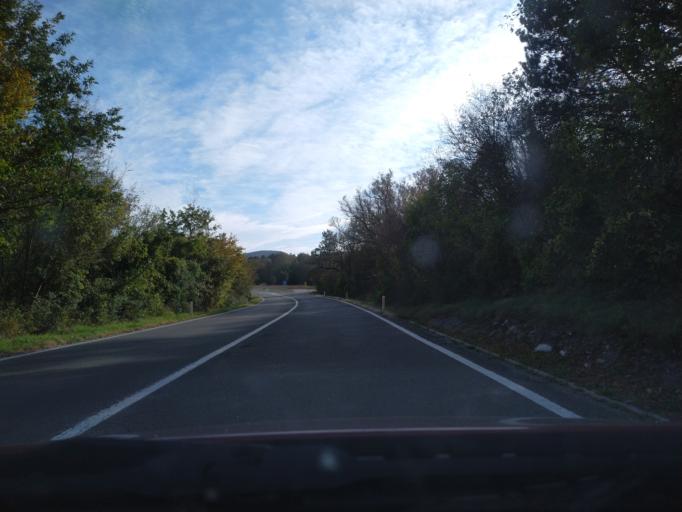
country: SI
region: Divaca
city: Divaca
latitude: 45.6655
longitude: 13.9725
